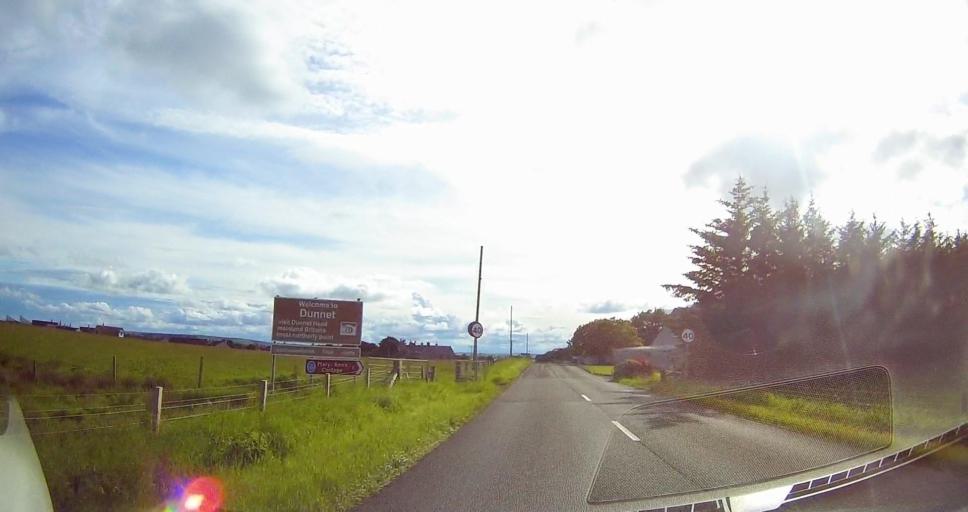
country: GB
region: Scotland
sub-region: Highland
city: Thurso
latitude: 58.6248
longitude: -3.3371
